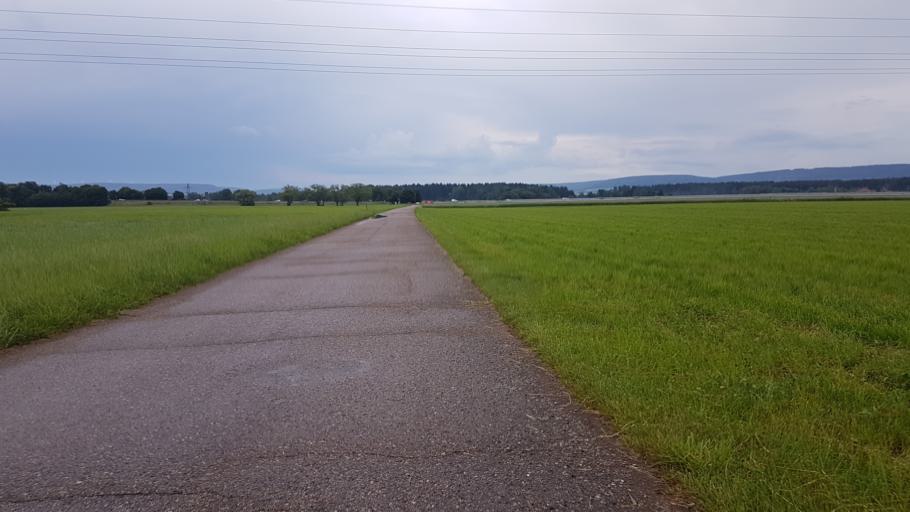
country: DE
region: Baden-Wuerttemberg
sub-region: Freiburg Region
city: Donaueschingen
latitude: 47.9395
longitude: 8.5102
